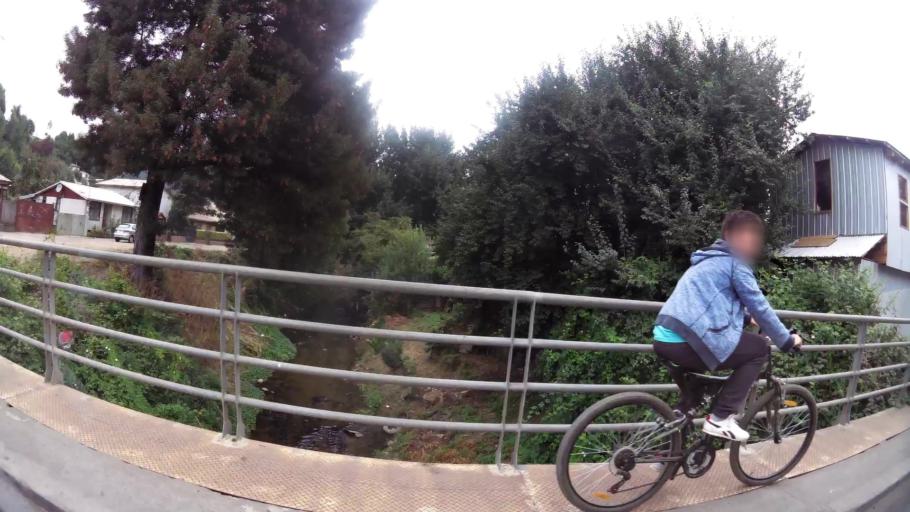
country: CL
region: Biobio
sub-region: Provincia de Concepcion
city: Concepcion
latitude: -36.8368
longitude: -73.0031
